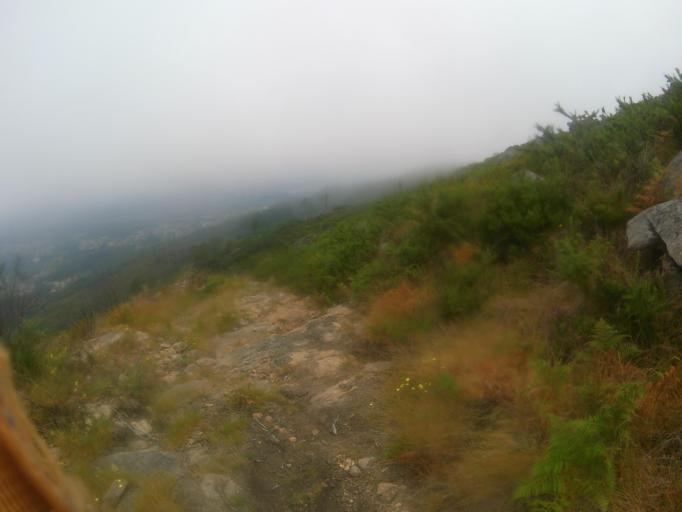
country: PT
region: Viana do Castelo
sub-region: Ponte de Lima
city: Ponte de Lima
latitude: 41.7133
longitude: -8.6013
